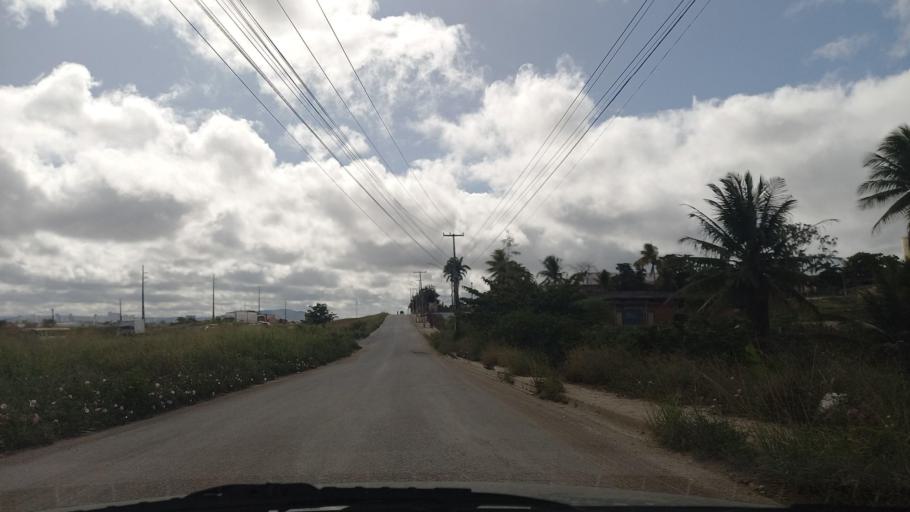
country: BR
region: Pernambuco
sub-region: Caruaru
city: Caruaru
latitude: -8.3071
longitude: -36.0178
